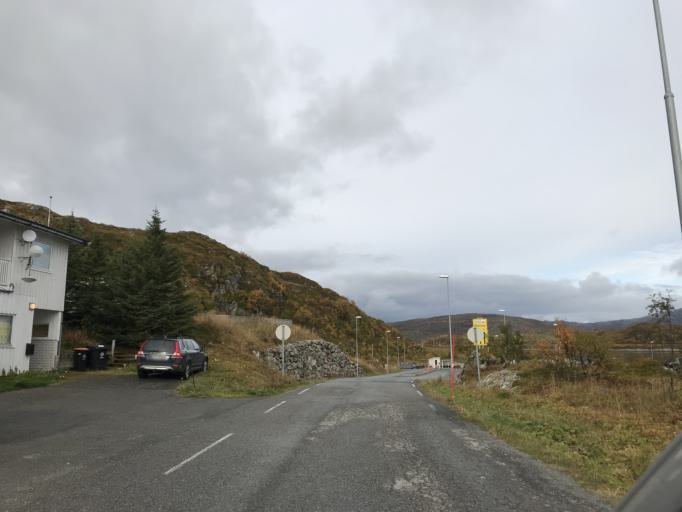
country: NO
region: Troms
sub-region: Tromso
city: Tromso
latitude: 70.0760
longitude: 18.9824
